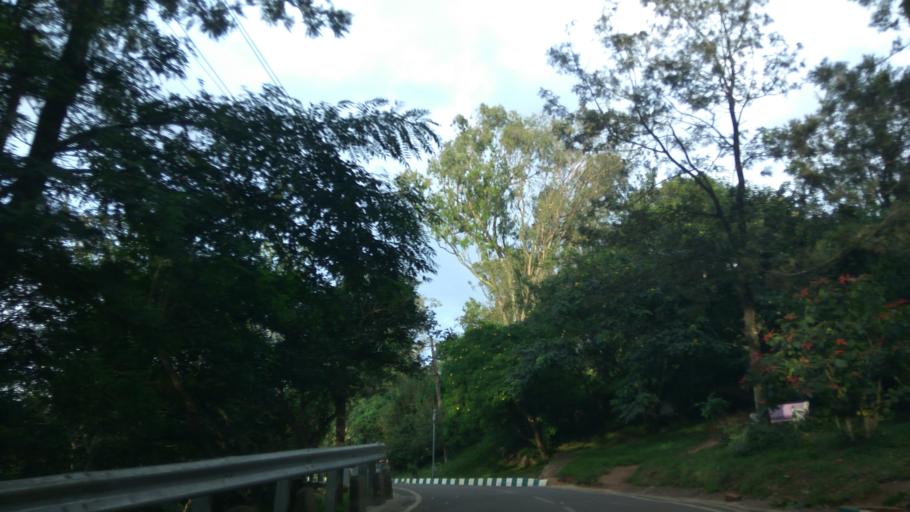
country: IN
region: Karnataka
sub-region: Chikkaballapur
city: Chik Ballapur
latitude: 13.3699
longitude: 77.6834
